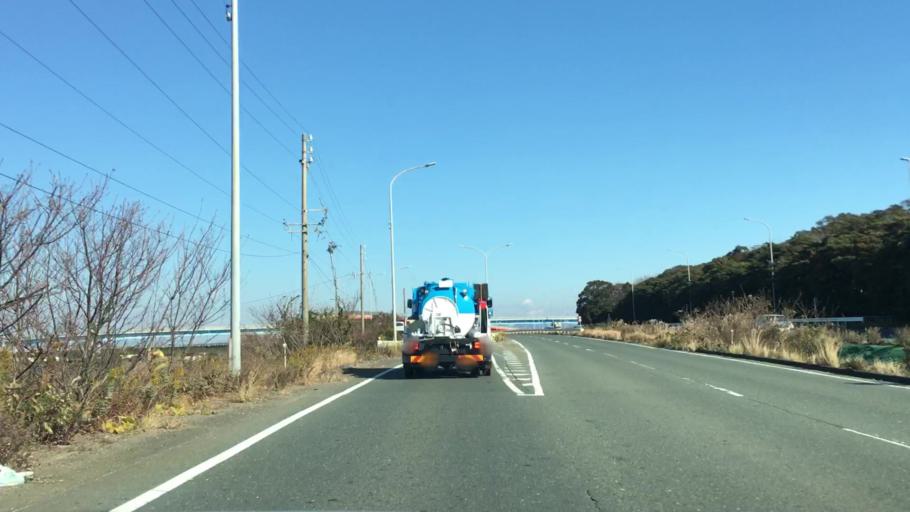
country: JP
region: Aichi
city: Toyohashi
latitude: 34.7257
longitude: 137.3455
